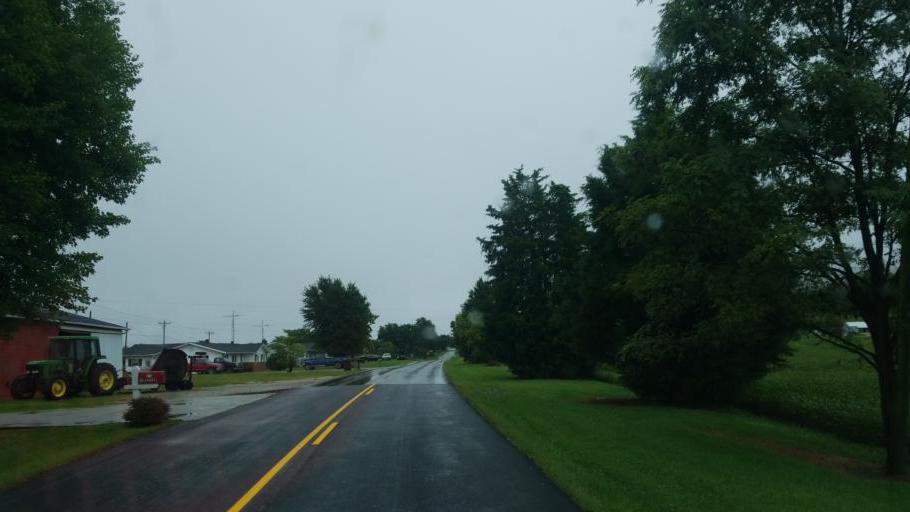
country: US
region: Kentucky
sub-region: Fleming County
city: Flemingsburg
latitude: 38.4847
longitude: -83.6114
